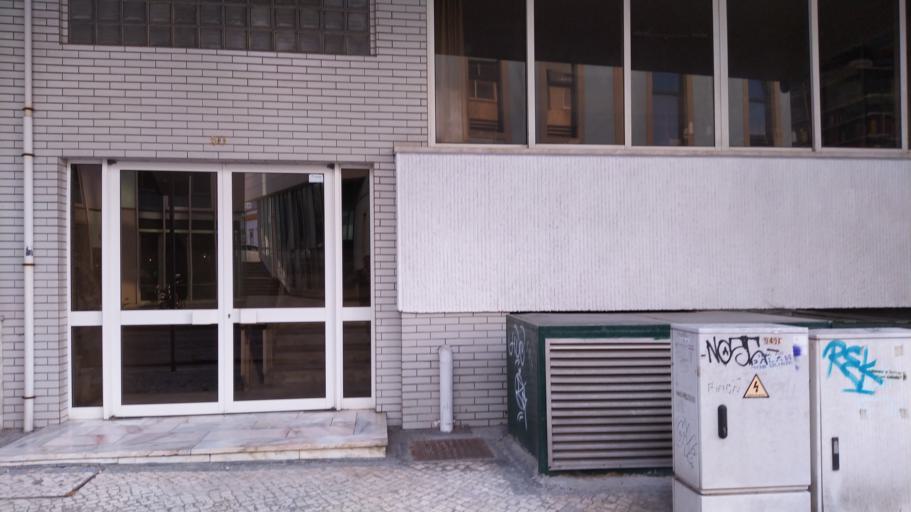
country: PT
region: Aveiro
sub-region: Aveiro
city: Aveiro
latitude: 40.6430
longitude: -8.6516
